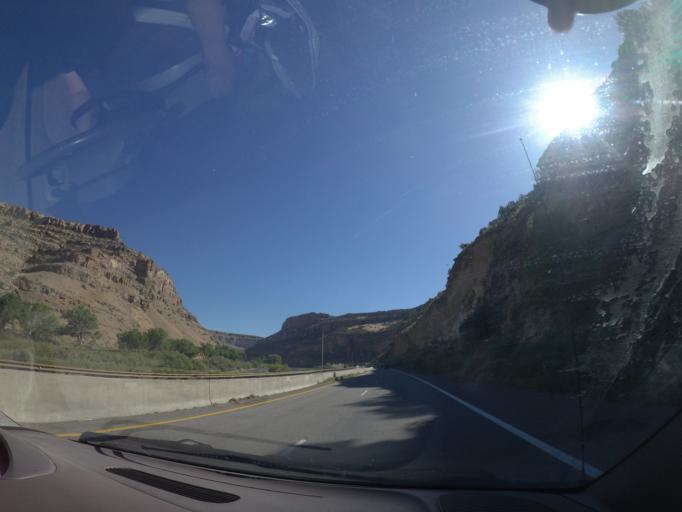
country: US
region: Colorado
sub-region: Mesa County
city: Palisade
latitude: 39.1776
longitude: -108.2851
